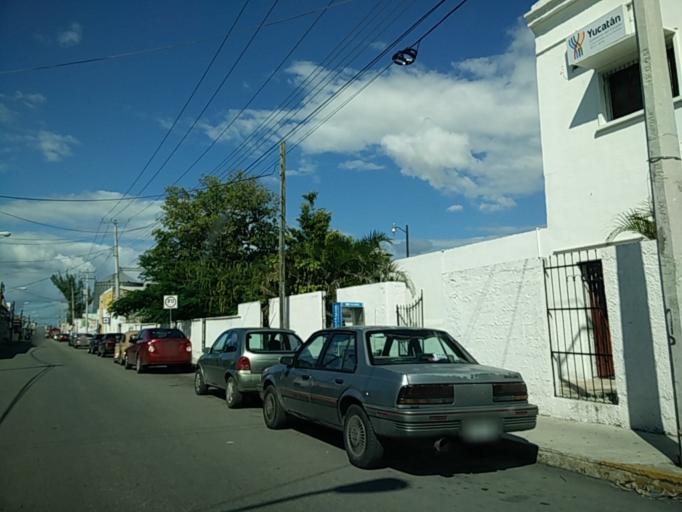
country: MX
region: Yucatan
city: Merida
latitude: 20.9770
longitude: -89.6155
